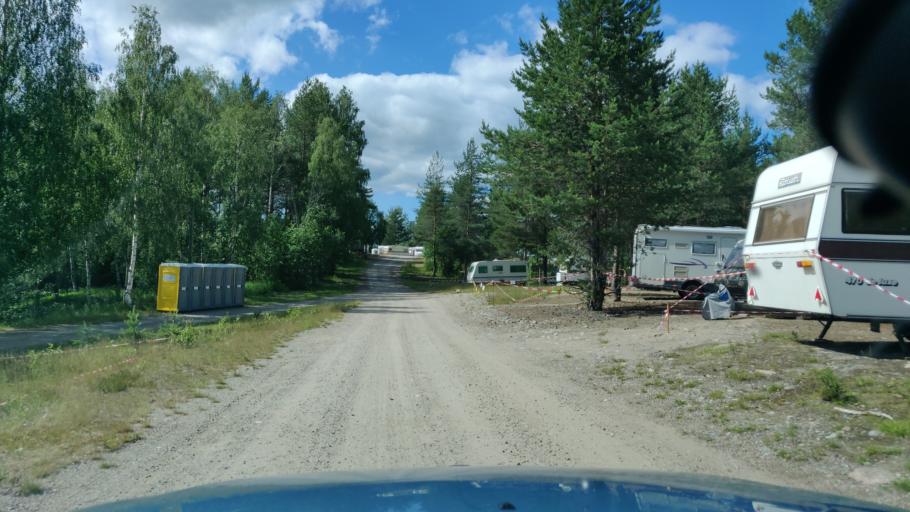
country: NO
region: Hedmark
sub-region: Trysil
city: Innbygda
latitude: 60.9121
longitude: 12.5613
